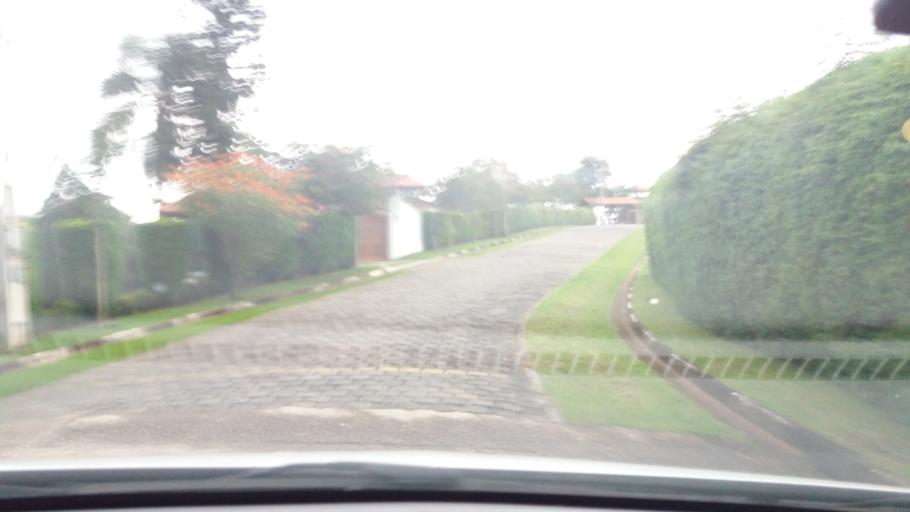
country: BR
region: Sao Paulo
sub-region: Bom Jesus Dos Perdoes
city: Bom Jesus dos Perdoes
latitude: -23.1678
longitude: -46.4639
